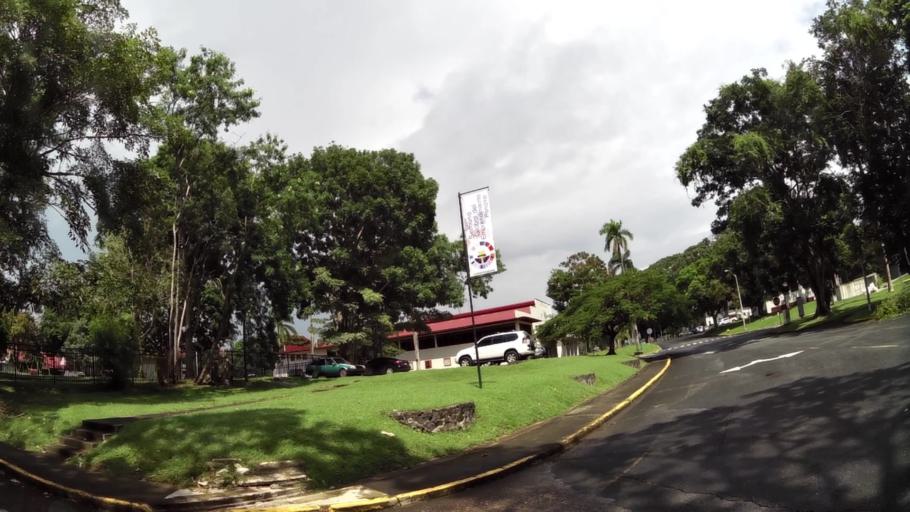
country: PA
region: Panama
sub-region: Distrito de Panama
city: Ancon
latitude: 8.9982
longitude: -79.5820
